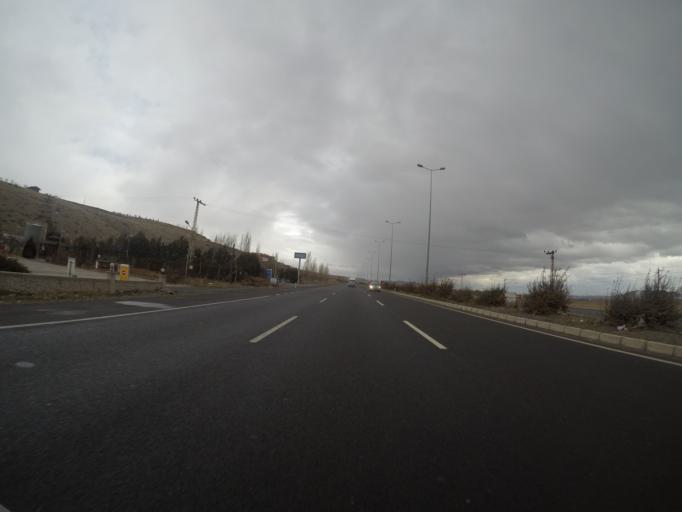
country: TR
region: Kayseri
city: Incesu
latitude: 38.7294
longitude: 35.2819
